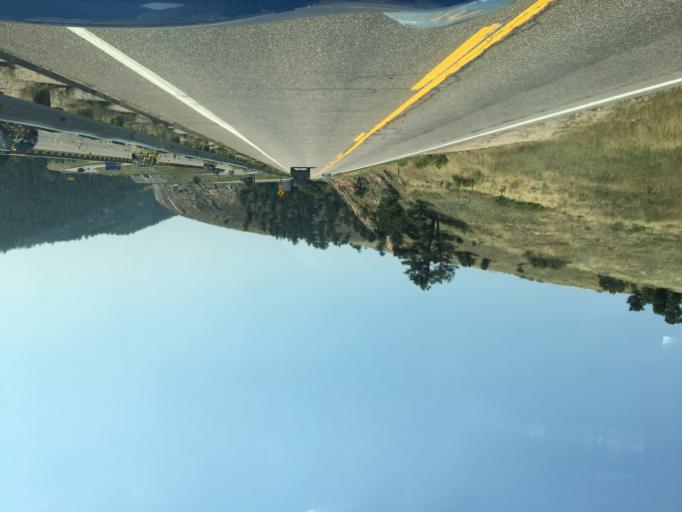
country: US
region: Colorado
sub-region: Jefferson County
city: Genesee
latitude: 39.7027
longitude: -105.2440
